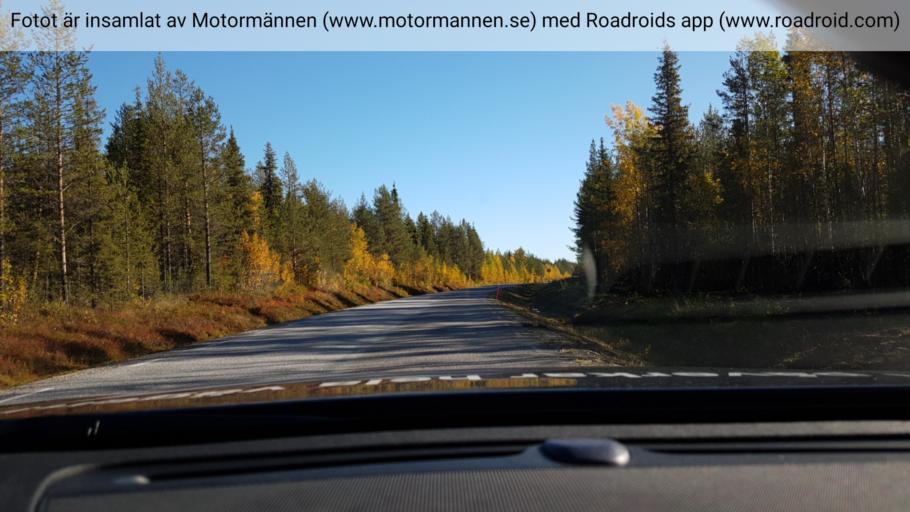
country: SE
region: Norrbotten
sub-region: Gallivare Kommun
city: Gaellivare
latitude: 66.4452
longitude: 20.7704
